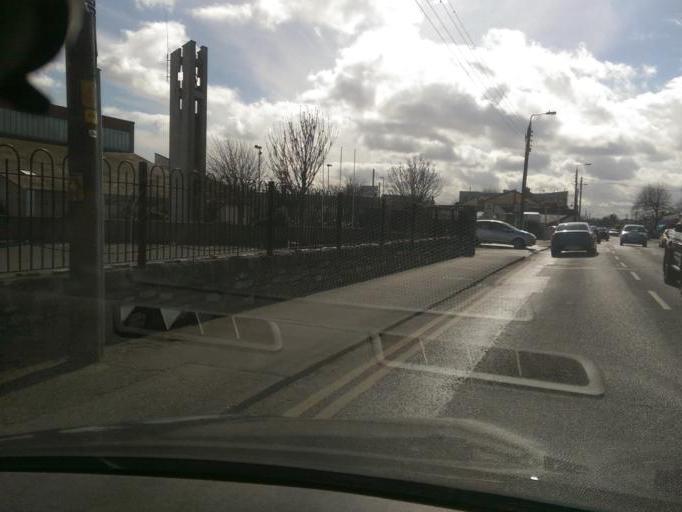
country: IE
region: Leinster
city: Portmarnock
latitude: 53.4221
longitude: -6.1356
